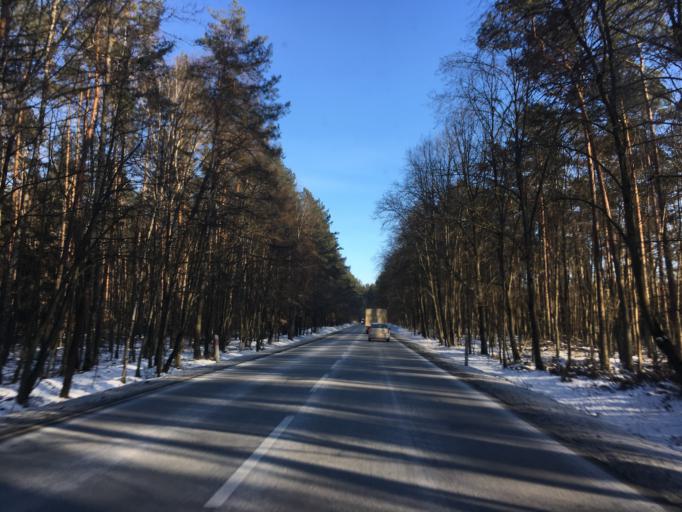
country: PL
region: Pomeranian Voivodeship
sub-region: Powiat koscierski
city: Koscierzyna
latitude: 54.1124
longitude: 17.9144
